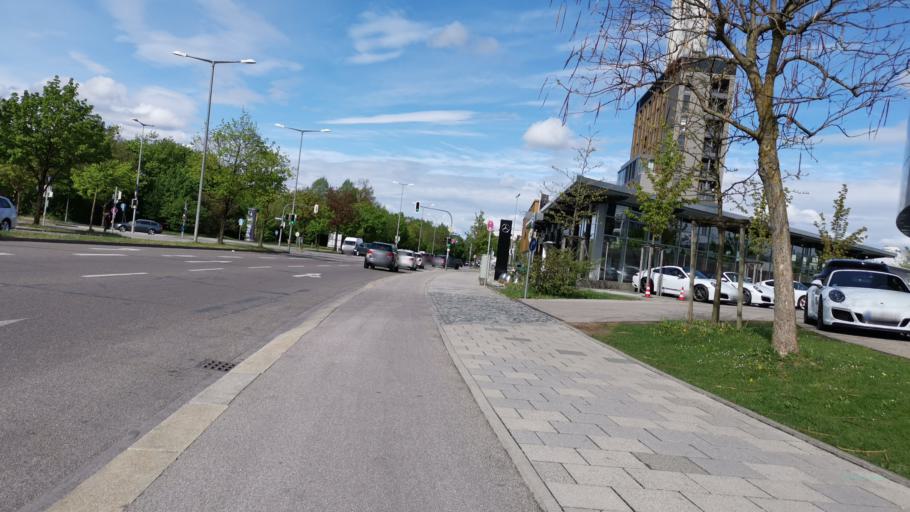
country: DE
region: Bavaria
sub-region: Upper Bavaria
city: Pullach im Isartal
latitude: 48.0937
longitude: 11.5035
